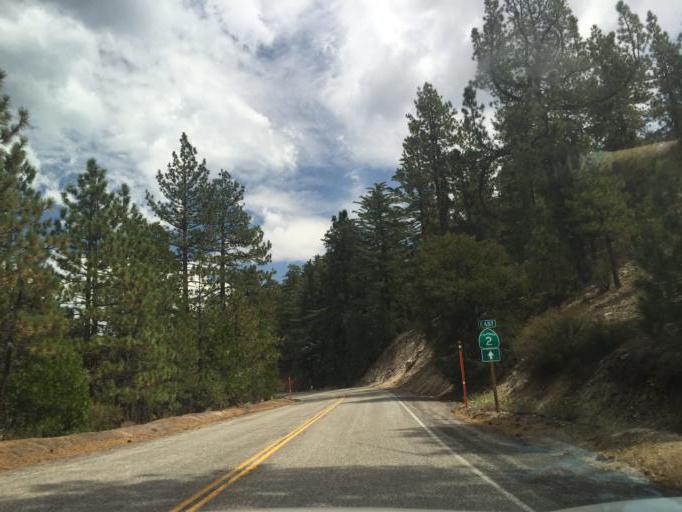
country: US
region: California
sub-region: Los Angeles County
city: Littlerock
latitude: 34.3432
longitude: -117.9818
